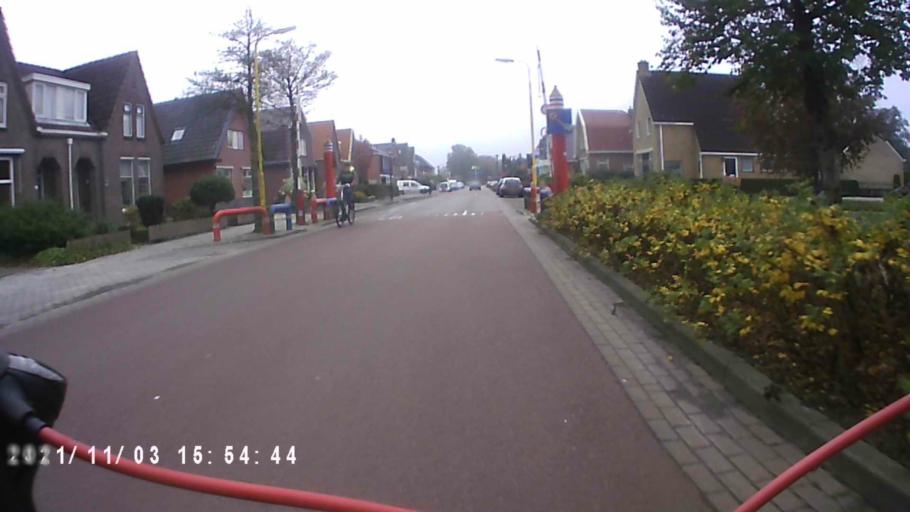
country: NL
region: Groningen
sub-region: Gemeente Leek
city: Leek
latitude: 53.0672
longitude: 6.3317
